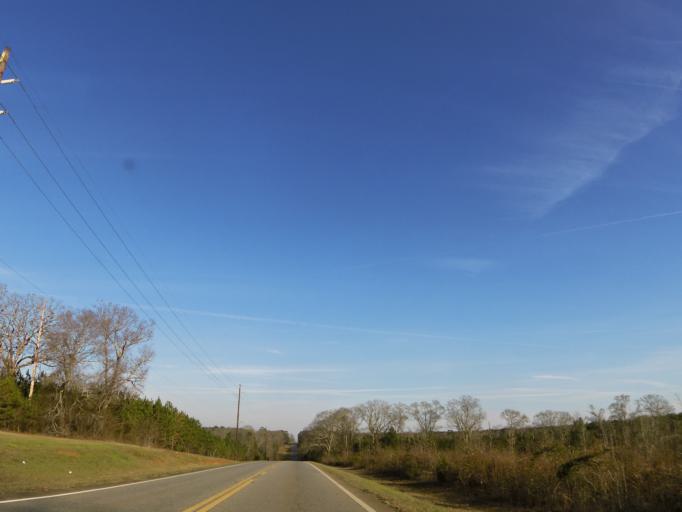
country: US
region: Georgia
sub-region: Webster County
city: Preston
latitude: 32.0342
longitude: -84.4246
